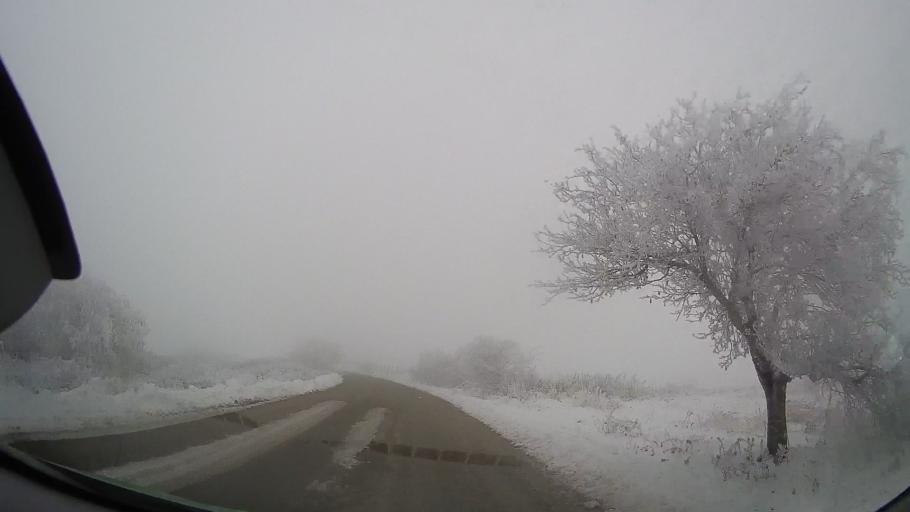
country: RO
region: Iasi
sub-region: Comuna Tansa
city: Suhulet
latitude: 46.8929
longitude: 27.2679
